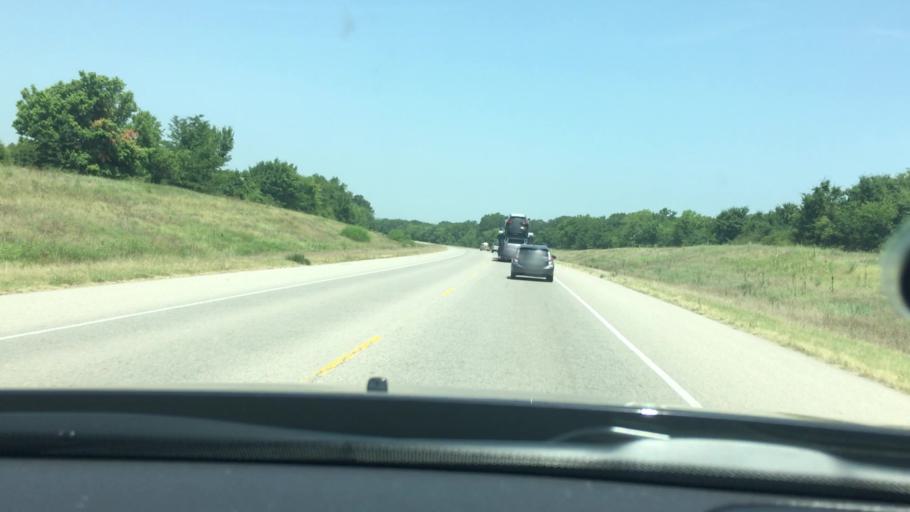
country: US
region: Oklahoma
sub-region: Pontotoc County
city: Ada
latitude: 34.6990
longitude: -96.6003
